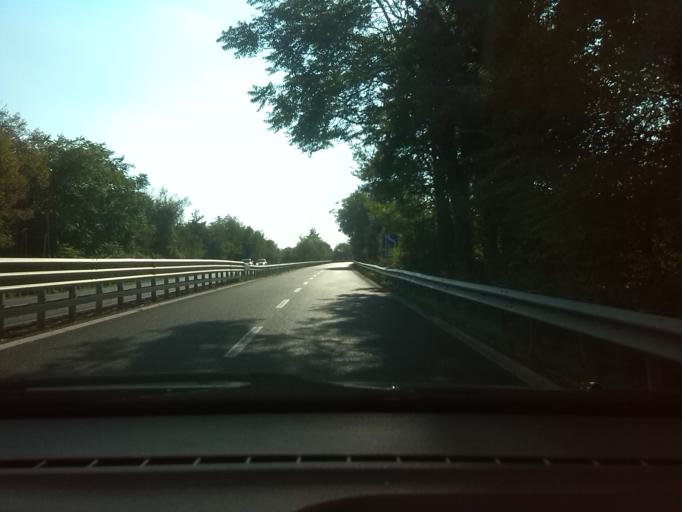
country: IT
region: Friuli Venezia Giulia
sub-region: Provincia di Trieste
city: Sistiana-Visogliano
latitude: 45.7640
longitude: 13.6429
